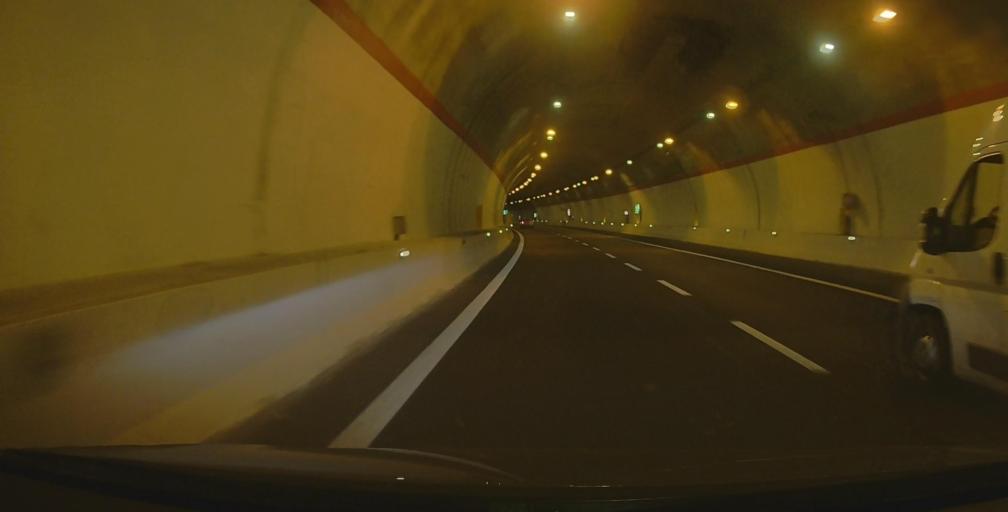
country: IT
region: Calabria
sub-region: Provincia di Cosenza
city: Morano Calabro
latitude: 39.8716
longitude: 16.1222
